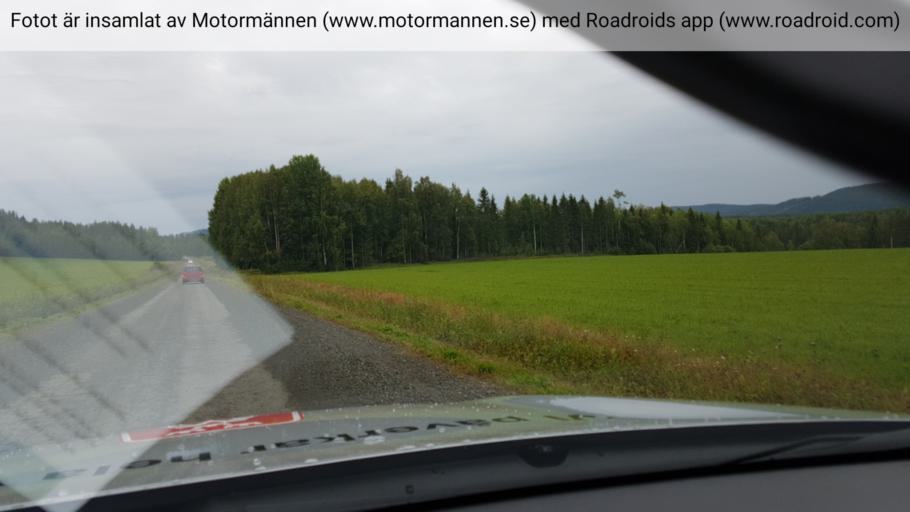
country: SE
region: Norrbotten
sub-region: Alvsbyns Kommun
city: AElvsbyn
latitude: 65.9824
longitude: 21.2117
